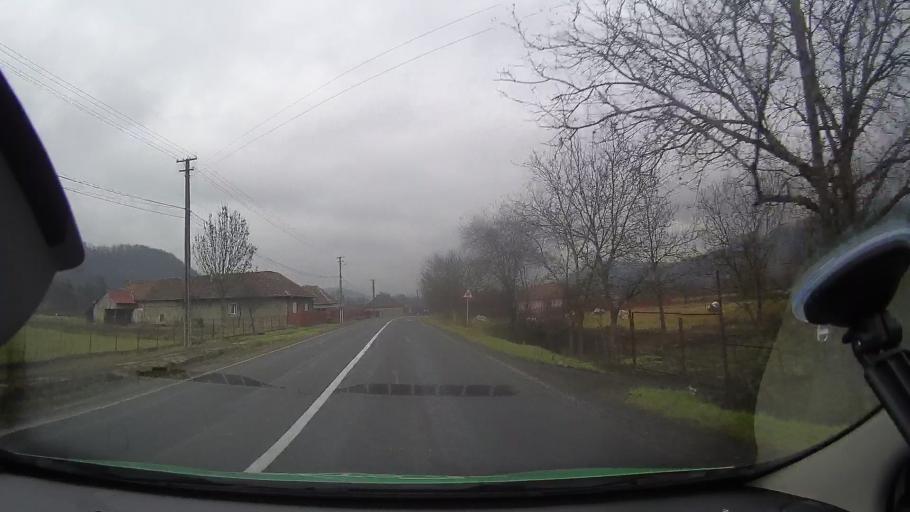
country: RO
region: Arad
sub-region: Comuna Plescuta
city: Plescuta
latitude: 46.2931
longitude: 22.3980
